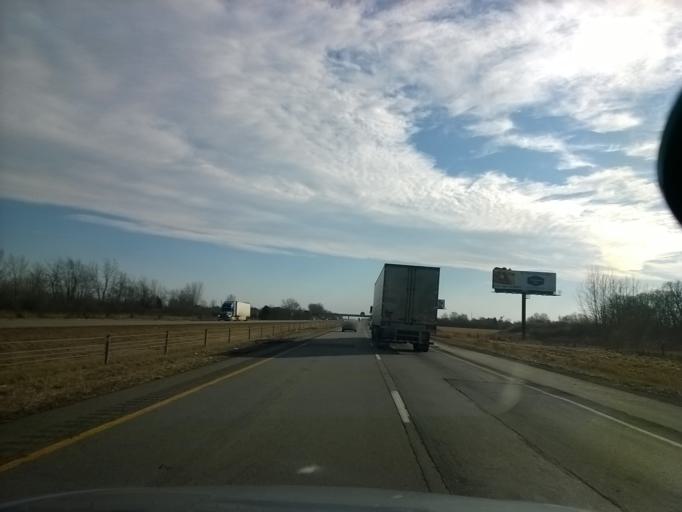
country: US
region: Indiana
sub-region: Johnson County
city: Franklin
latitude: 39.5017
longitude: -86.0192
